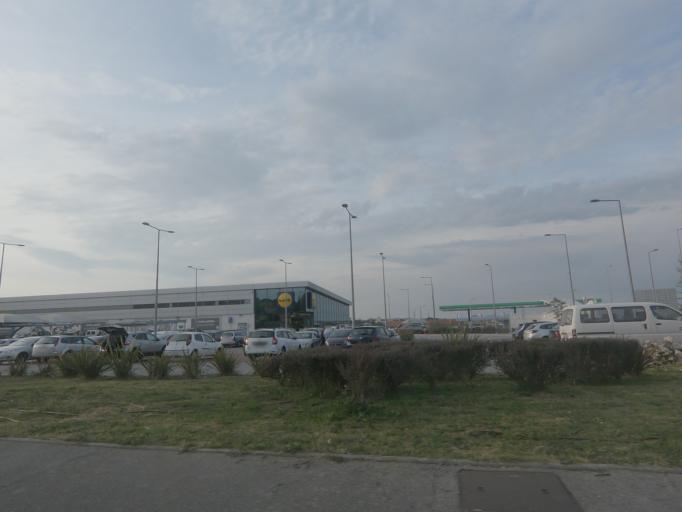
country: PT
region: Porto
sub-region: Matosinhos
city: Sao Mamede de Infesta
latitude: 41.1986
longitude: -8.6096
